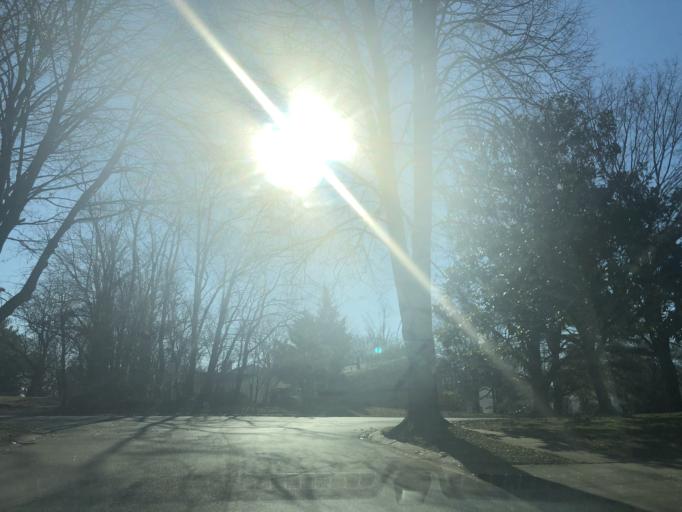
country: US
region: Maryland
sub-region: Howard County
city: Columbia
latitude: 39.1952
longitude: -76.8386
